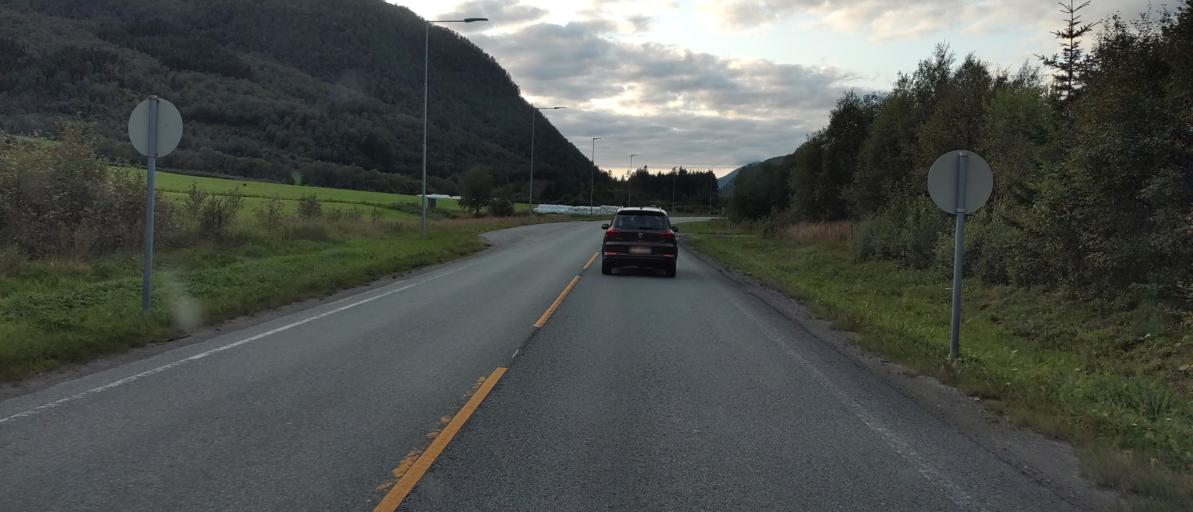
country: NO
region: More og Romsdal
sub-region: Molde
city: Molde
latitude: 62.7892
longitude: 7.2354
